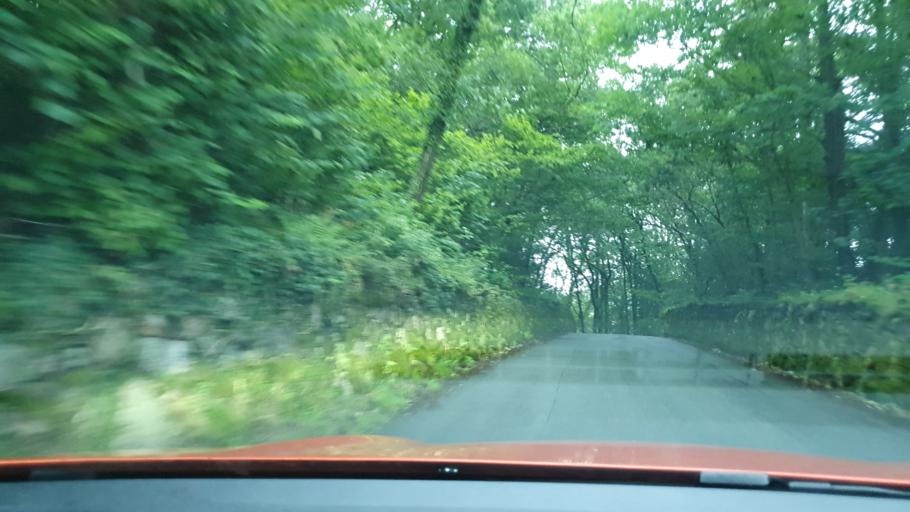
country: GB
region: England
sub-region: Cumbria
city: Seascale
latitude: 54.3869
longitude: -3.3158
